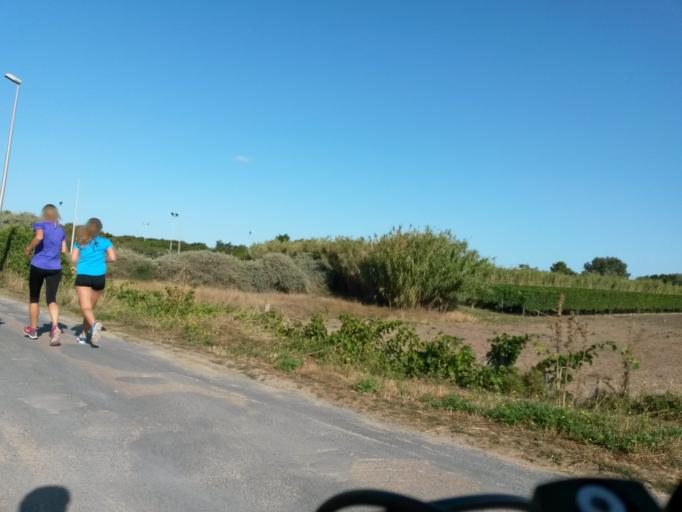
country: FR
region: Poitou-Charentes
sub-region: Departement de la Charente-Maritime
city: Sainte-Marie-de-Re
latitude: 46.1497
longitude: -1.3282
